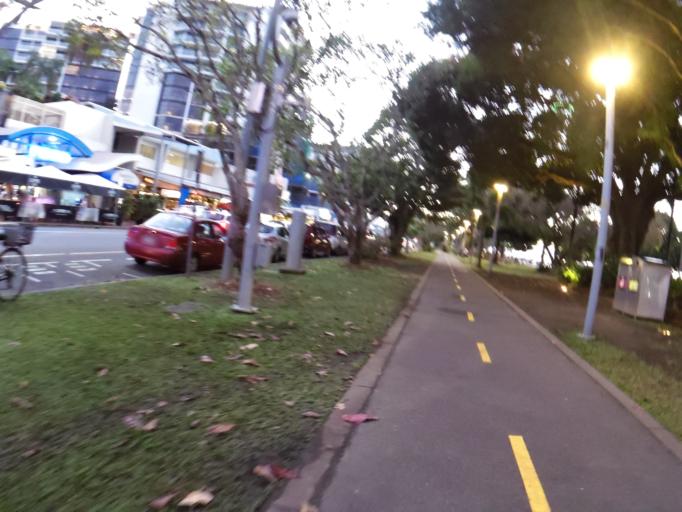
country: AU
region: Queensland
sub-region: Cairns
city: Cairns
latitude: -16.9198
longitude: 145.7773
